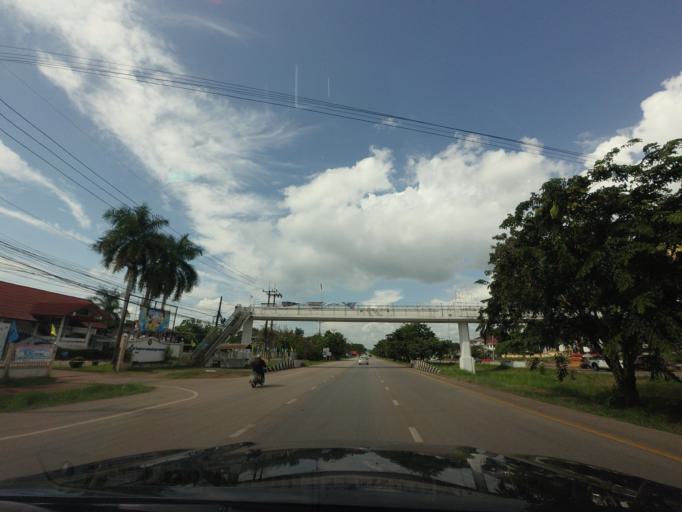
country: TH
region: Nong Khai
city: Sa Khrai
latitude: 17.5520
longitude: 102.8008
